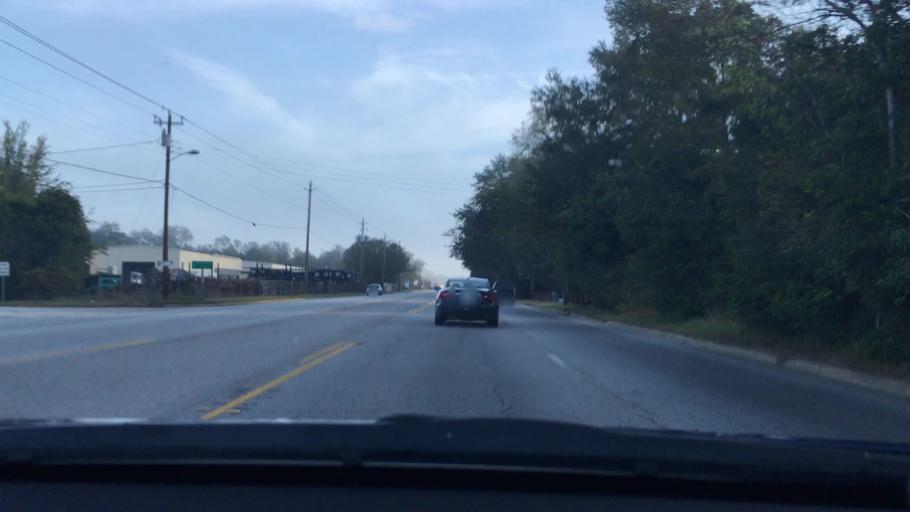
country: US
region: South Carolina
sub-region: Sumter County
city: South Sumter
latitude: 33.8904
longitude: -80.3436
